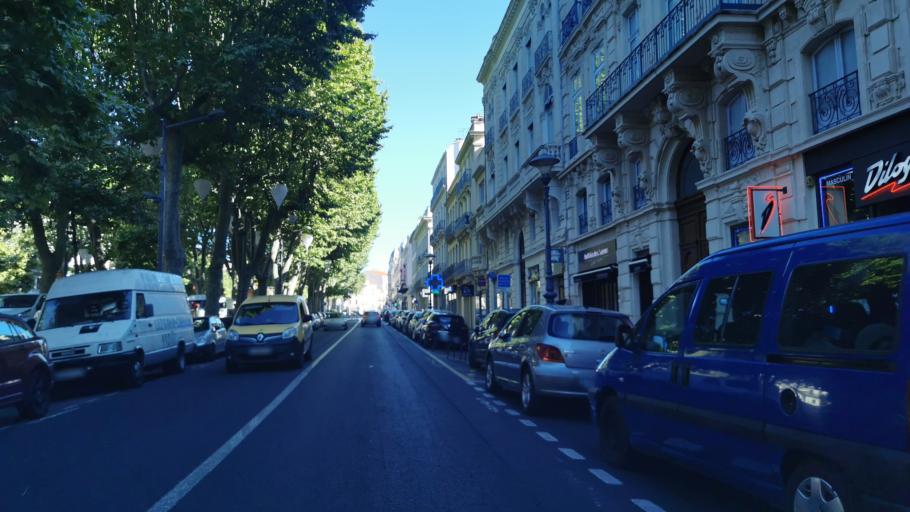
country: FR
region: Languedoc-Roussillon
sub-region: Departement de l'Herault
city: Beziers
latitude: 43.3426
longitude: 3.2172
